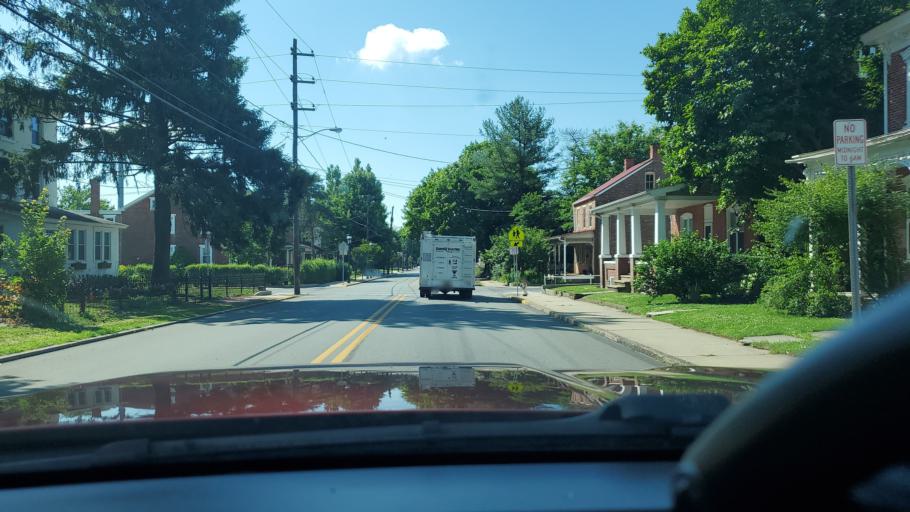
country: US
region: Pennsylvania
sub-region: Montgomery County
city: East Greenville
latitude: 40.4094
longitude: -75.5049
